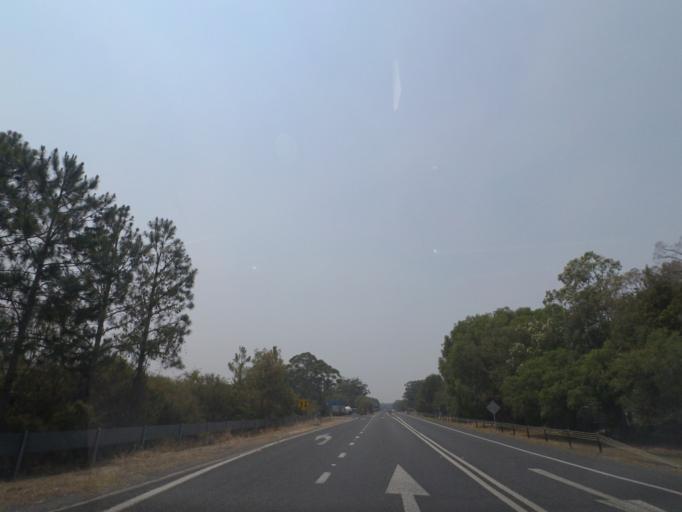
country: AU
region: New South Wales
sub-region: Ballina
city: Ballina
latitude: -28.9360
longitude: 153.4713
